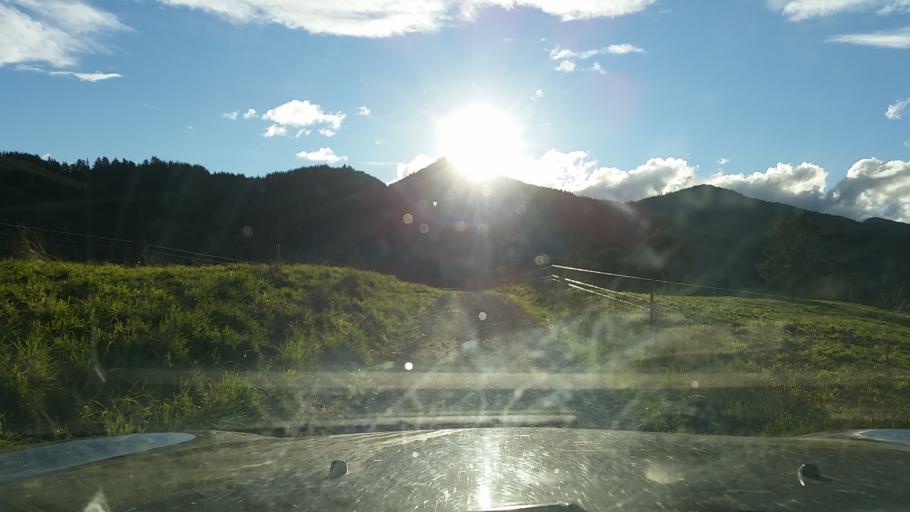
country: NZ
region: Nelson
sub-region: Nelson City
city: Nelson
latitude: -41.5392
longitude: 173.4949
